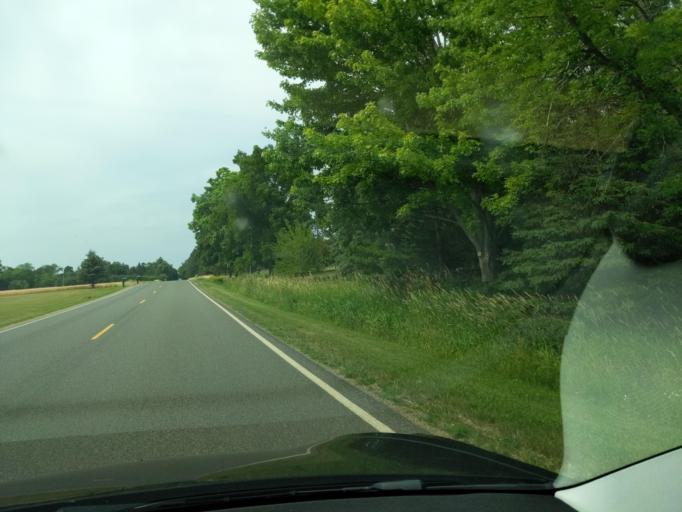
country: US
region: Michigan
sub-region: Clinton County
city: DeWitt
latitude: 42.8732
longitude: -84.6024
